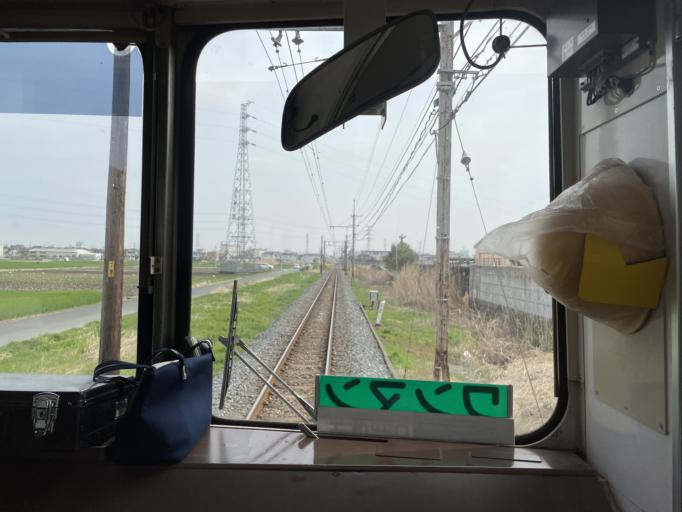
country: JP
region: Saitama
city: Kumagaya
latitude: 36.1365
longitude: 139.4202
